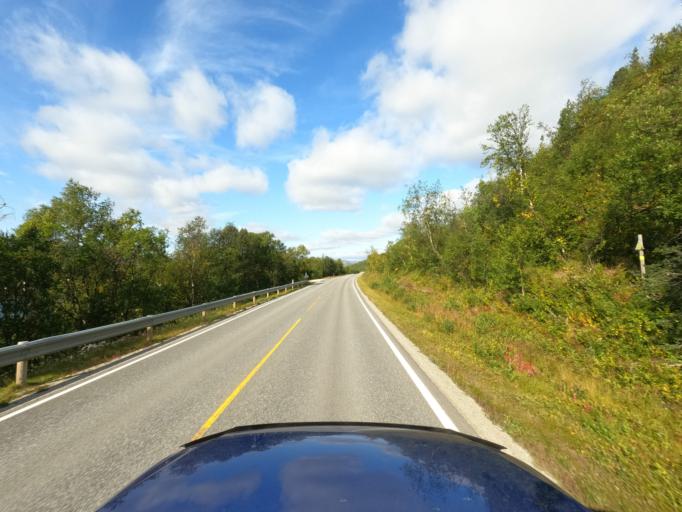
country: NO
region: Finnmark Fylke
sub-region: Porsanger
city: Lakselv
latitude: 69.9308
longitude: 24.9789
